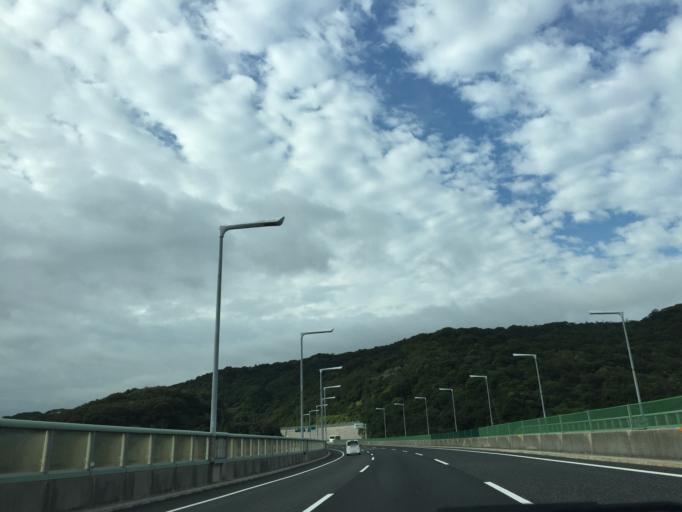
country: JP
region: Hyogo
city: Akashi
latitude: 34.6018
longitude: 135.0083
